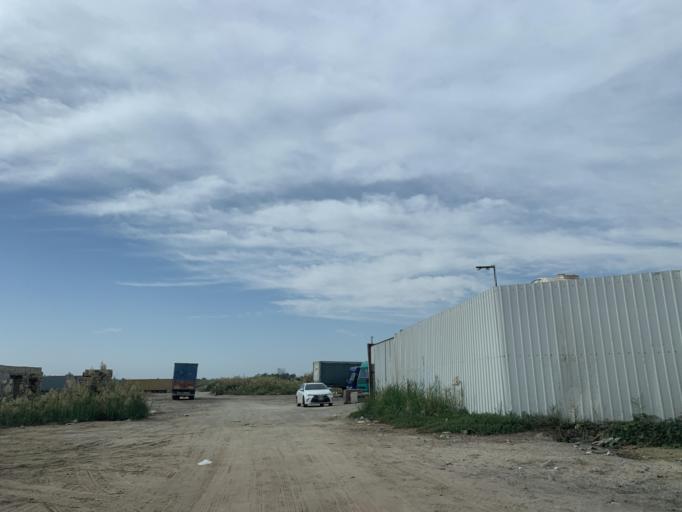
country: BH
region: Central Governorate
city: Madinat Hamad
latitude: 26.1130
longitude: 50.4779
